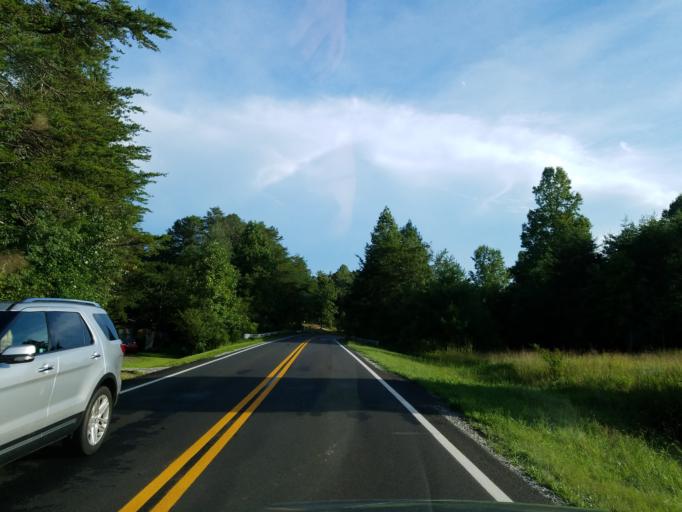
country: US
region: Georgia
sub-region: Lumpkin County
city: Dahlonega
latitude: 34.5834
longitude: -83.8857
